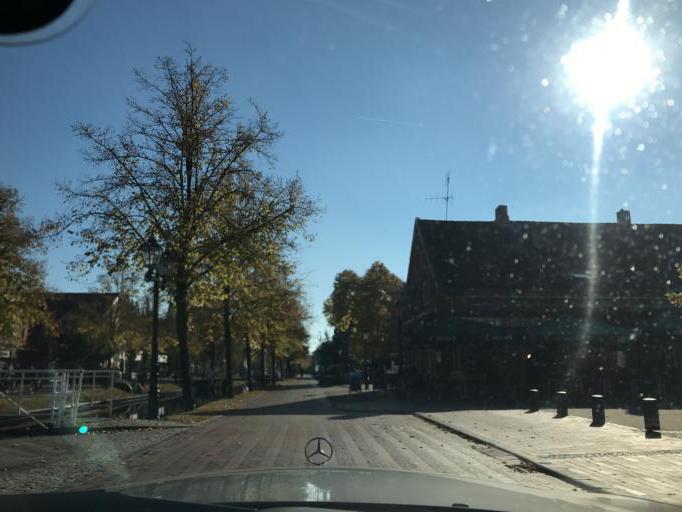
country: DE
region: Lower Saxony
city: Papenburg
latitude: 53.0837
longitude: 7.3902
